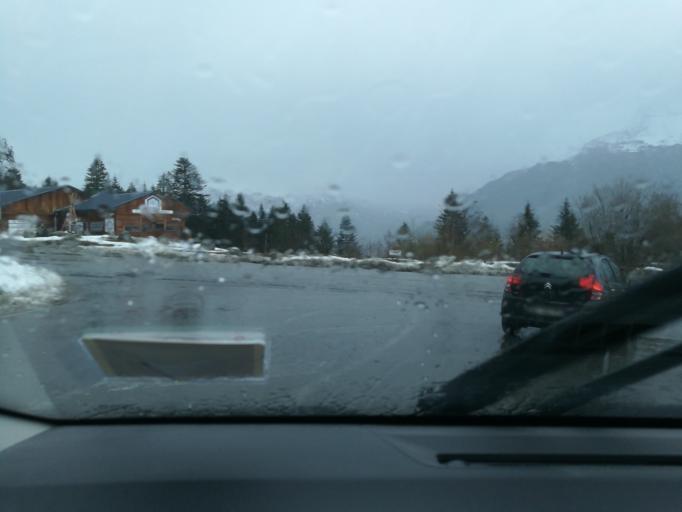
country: FR
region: Rhone-Alpes
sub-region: Departement de la Haute-Savoie
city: Saint-Gervais-les-Bains
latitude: 45.8942
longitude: 6.6966
